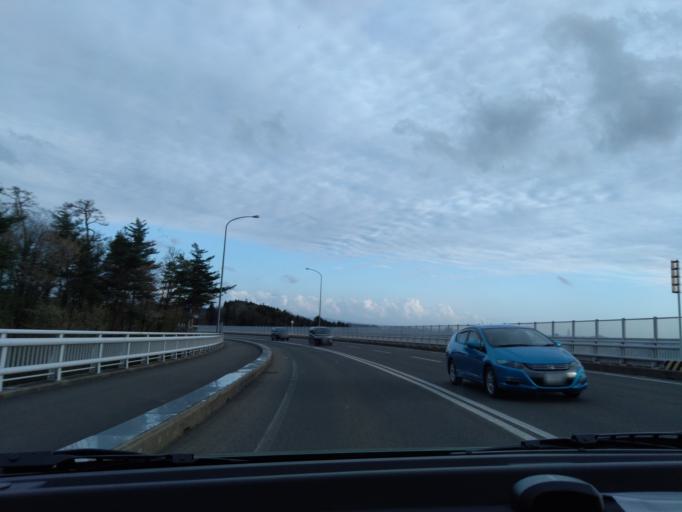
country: JP
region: Akita
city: Akita
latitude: 39.7360
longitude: 140.1365
